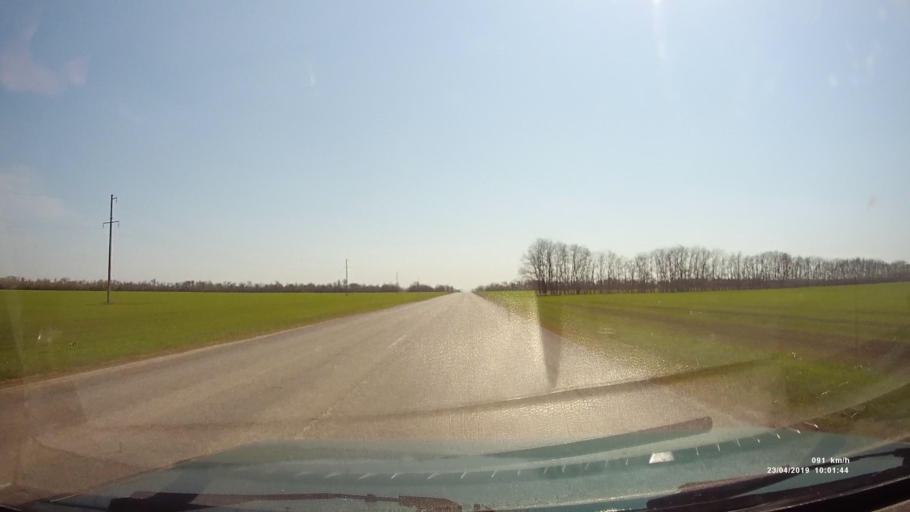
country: RU
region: Rostov
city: Sovetskoye
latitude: 46.7641
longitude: 42.1558
